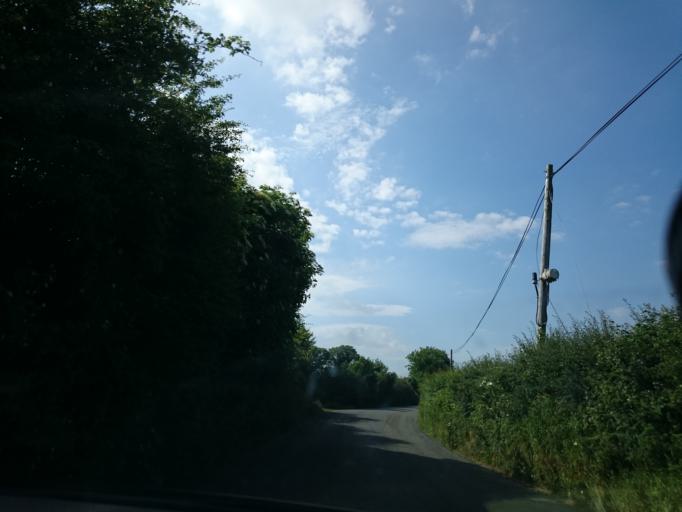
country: IE
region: Leinster
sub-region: Kilkenny
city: Thomastown
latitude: 52.5258
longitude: -7.2043
